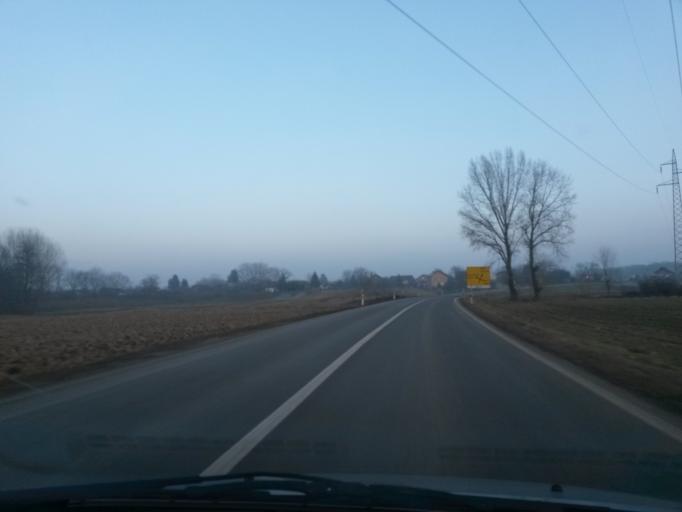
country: HR
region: Varazdinska
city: Ludbreg
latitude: 46.2555
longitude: 16.6310
